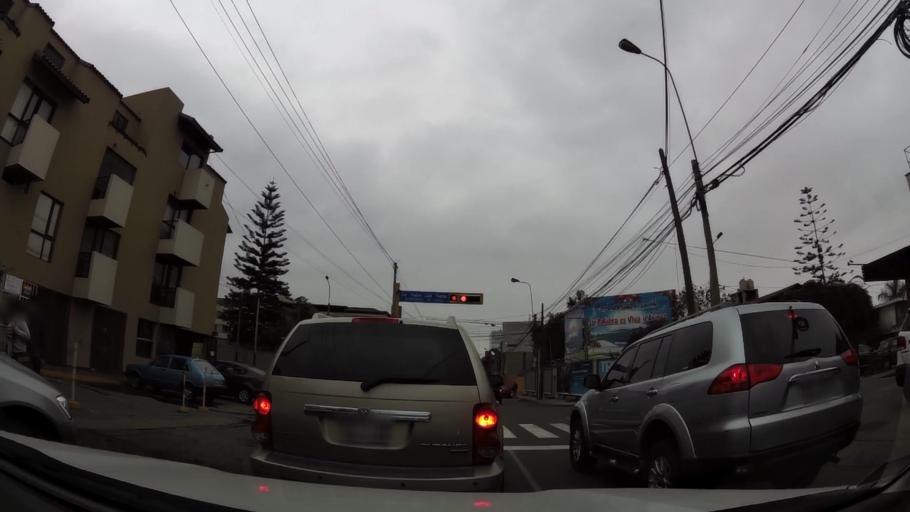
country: PE
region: Lima
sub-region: Lima
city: La Molina
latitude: -12.1023
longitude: -76.9720
